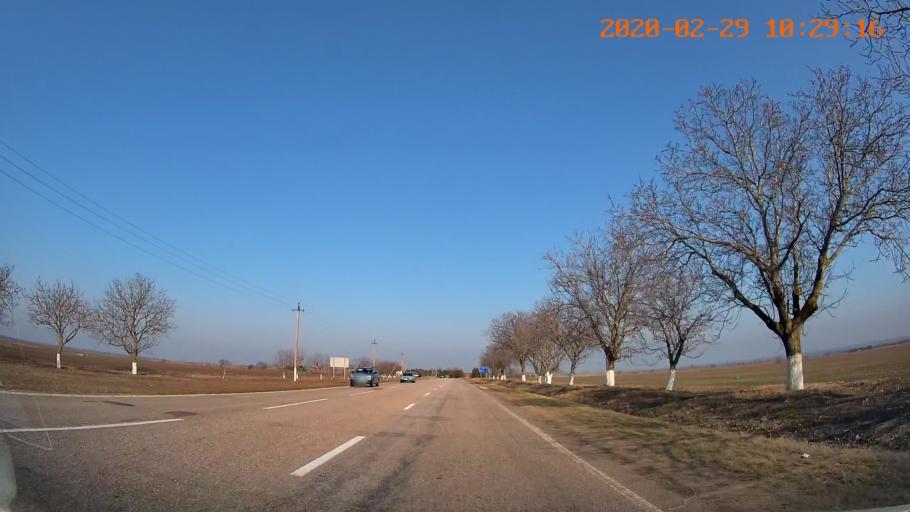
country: MD
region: Telenesti
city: Tiraspolul Nou
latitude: 46.9214
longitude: 29.5867
